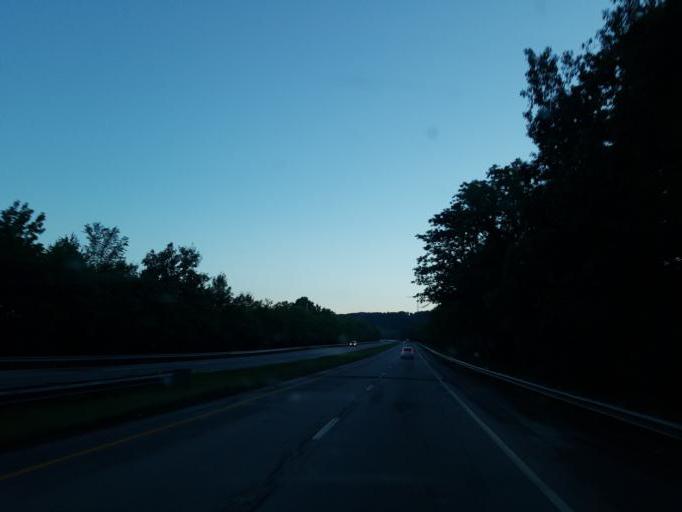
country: US
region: Ohio
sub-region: Summit County
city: Clinton
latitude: 40.9195
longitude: -81.6482
